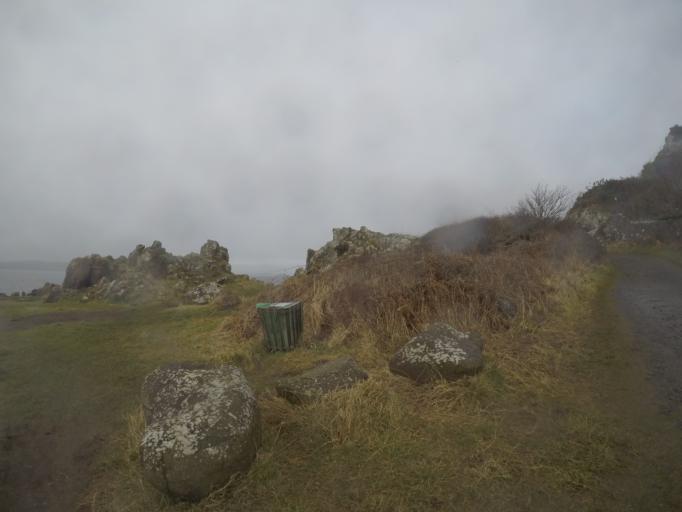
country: GB
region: Scotland
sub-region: North Ayrshire
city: Millport
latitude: 55.7020
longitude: -4.9046
